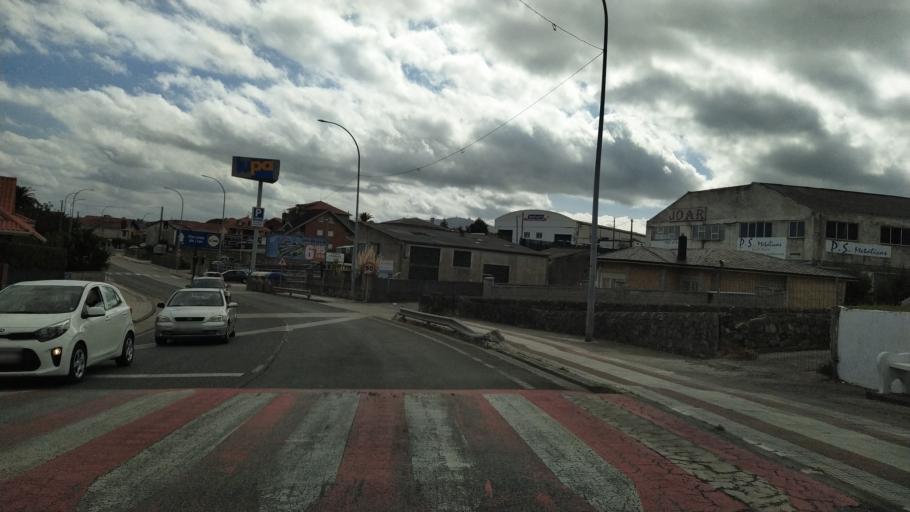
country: ES
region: Cantabria
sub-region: Provincia de Cantabria
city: Camargo
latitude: 43.4224
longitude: -3.8520
